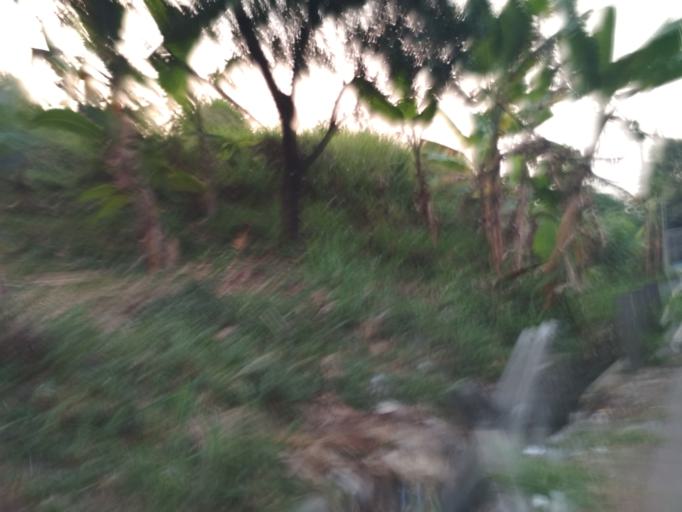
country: ID
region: West Java
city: Caringin
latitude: -6.6661
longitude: 106.8458
